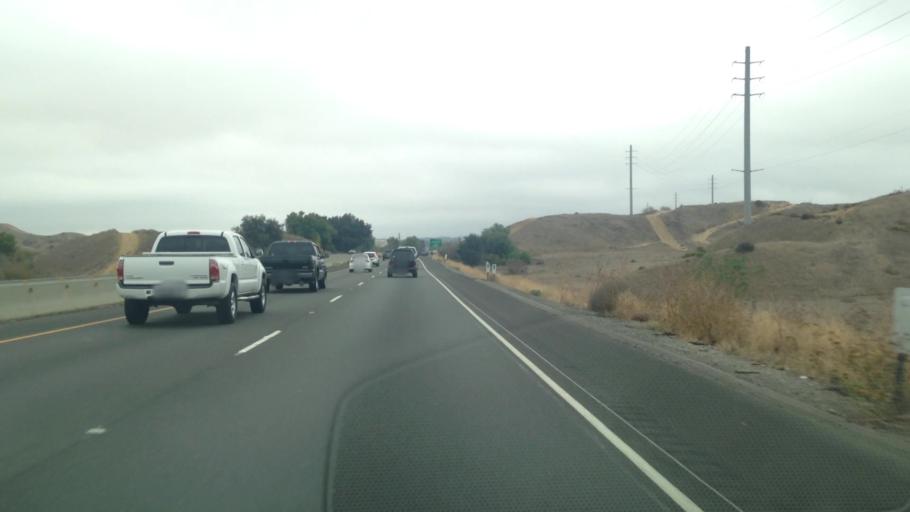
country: US
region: California
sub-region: Riverside County
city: Calimesa
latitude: 33.9401
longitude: -117.0447
